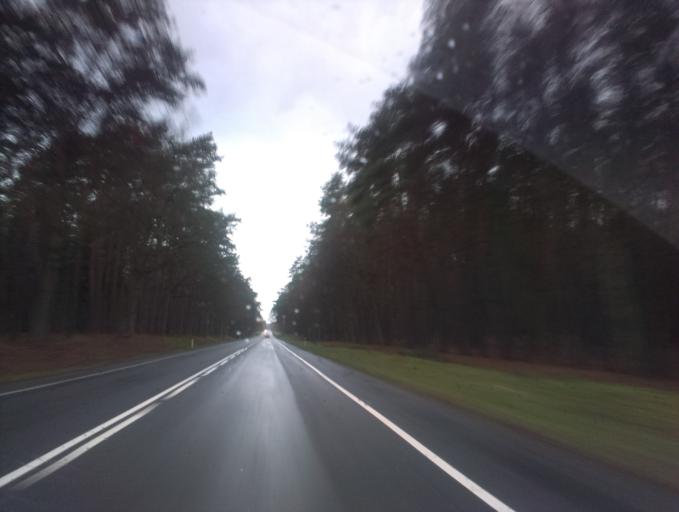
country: PL
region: Greater Poland Voivodeship
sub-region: Powiat chodzieski
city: Chodziez
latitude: 53.0052
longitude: 16.8599
